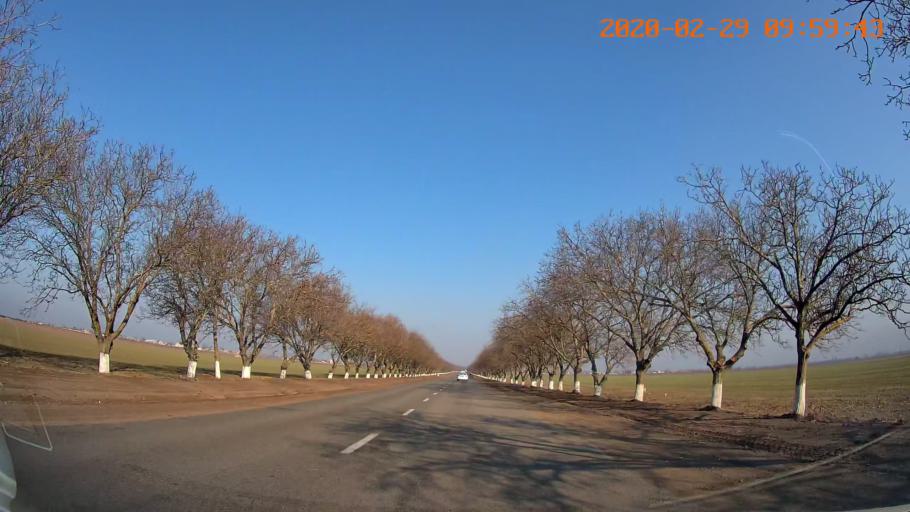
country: MD
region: Telenesti
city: Slobozia
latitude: 46.7599
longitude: 29.6878
